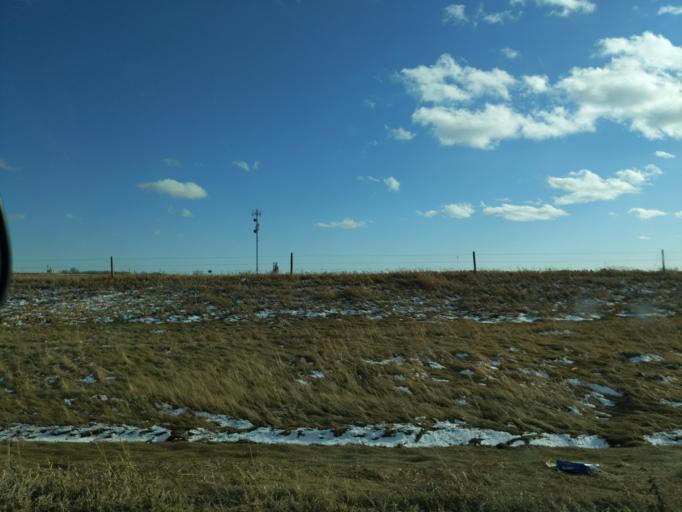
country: CA
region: Saskatchewan
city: Lloydminster
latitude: 53.2752
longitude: -109.9731
